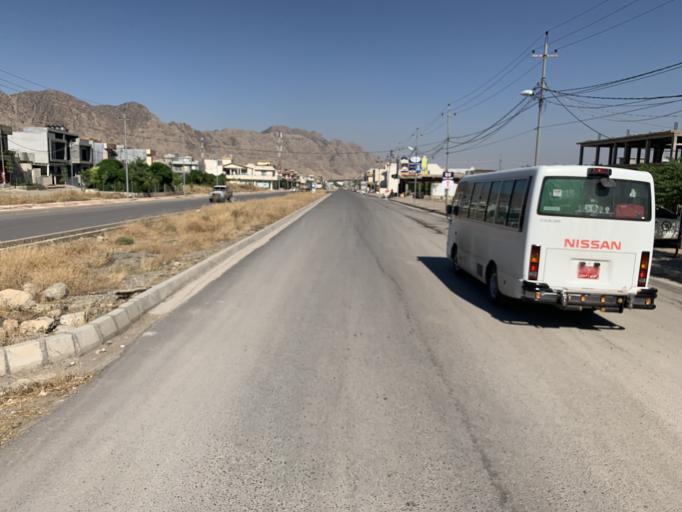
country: IQ
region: As Sulaymaniyah
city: Raniye
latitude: 36.2596
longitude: 44.8620
